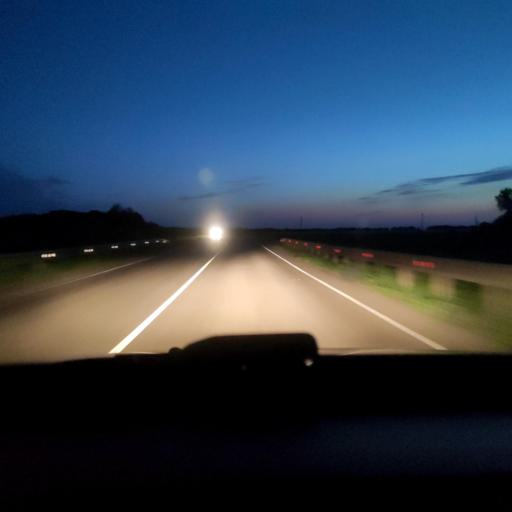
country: RU
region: Voronezj
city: Panino
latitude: 51.5738
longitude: 39.9116
